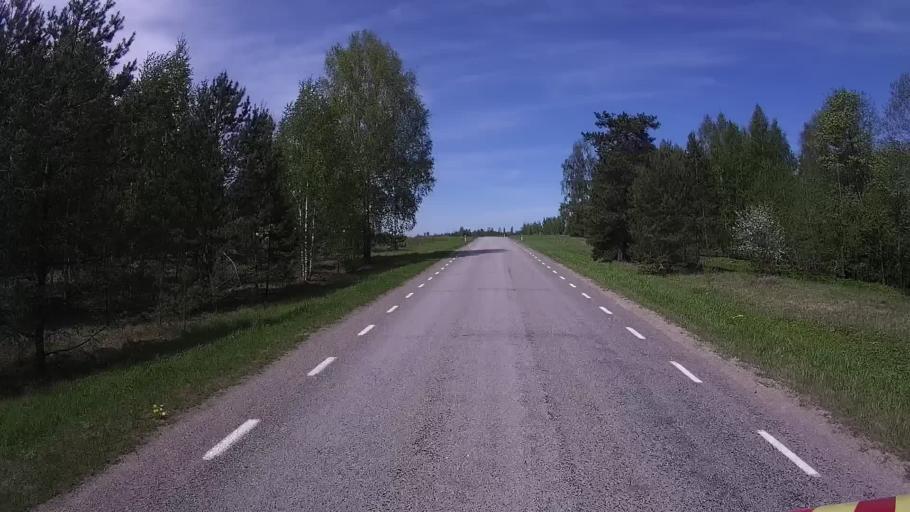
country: EE
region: Vorumaa
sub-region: Antsla vald
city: Vana-Antsla
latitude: 57.6320
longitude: 26.3405
